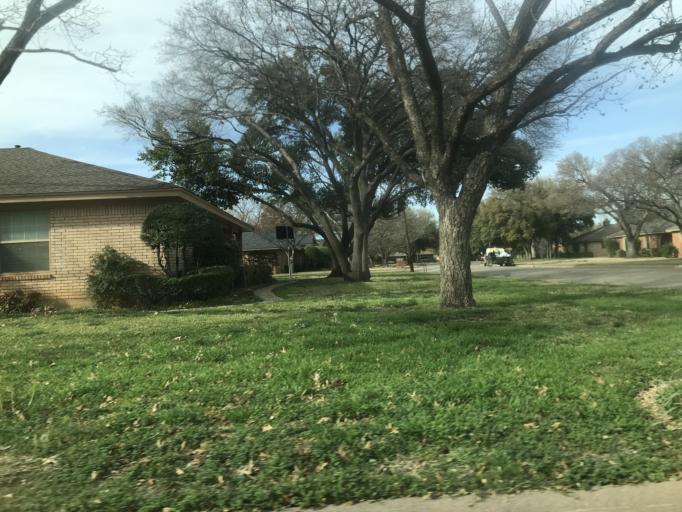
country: US
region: Texas
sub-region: Taylor County
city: Abilene
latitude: 32.4143
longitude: -99.7704
